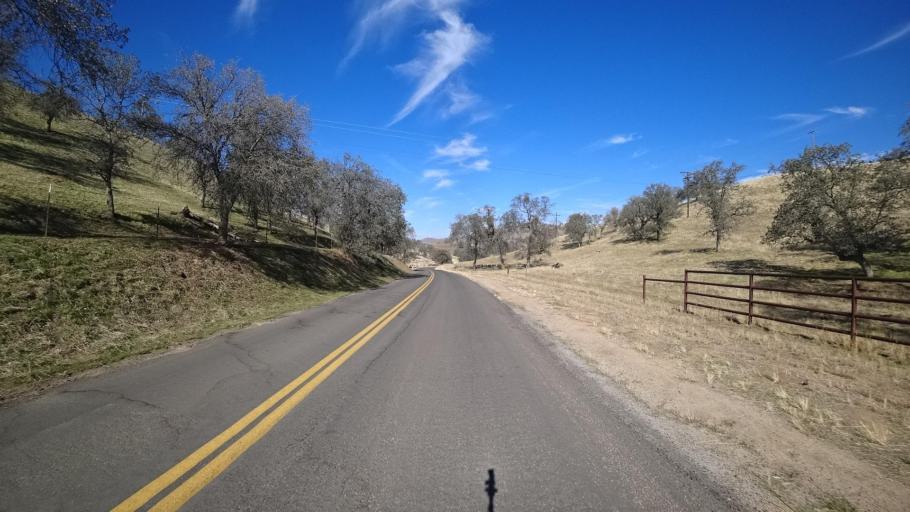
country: US
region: California
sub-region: Kern County
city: Oildale
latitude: 35.6478
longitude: -118.8404
